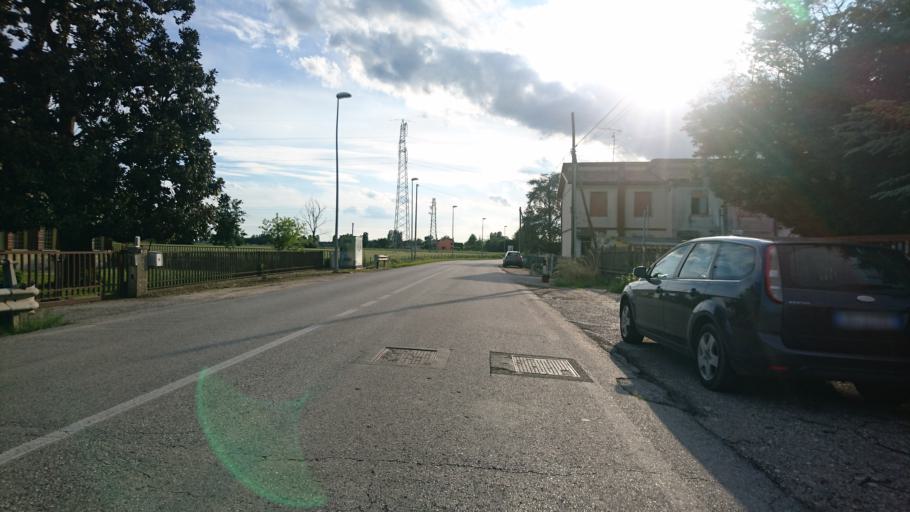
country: IT
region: Veneto
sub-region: Provincia di Rovigo
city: Trecenta
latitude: 45.0270
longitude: 11.4518
